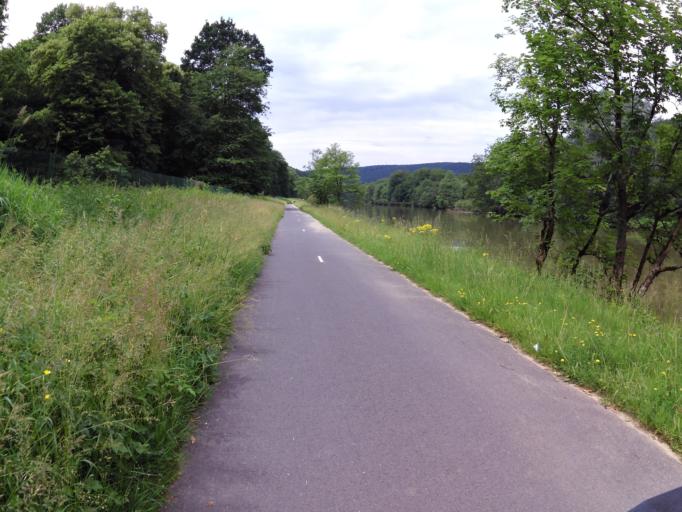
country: FR
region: Champagne-Ardenne
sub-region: Departement des Ardennes
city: Nouzonville
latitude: 49.8025
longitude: 4.7514
